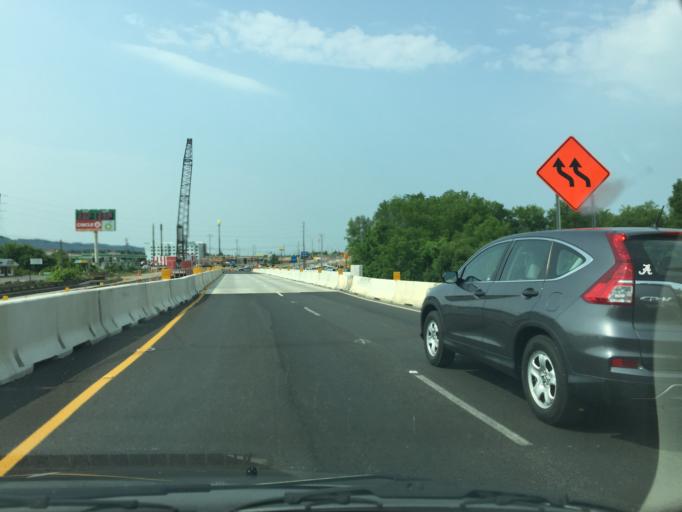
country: US
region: Georgia
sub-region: Catoosa County
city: Ringgold
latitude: 34.9157
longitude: -85.1239
